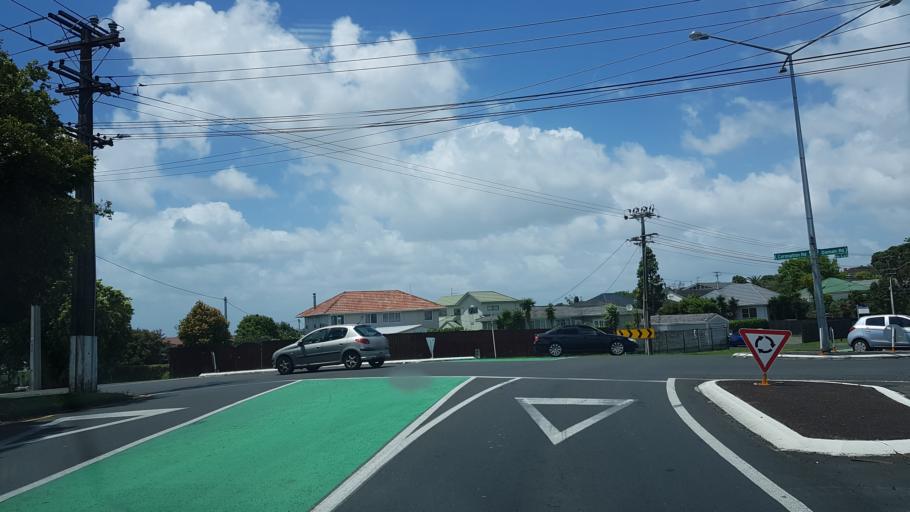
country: NZ
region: Auckland
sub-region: Auckland
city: North Shore
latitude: -36.7923
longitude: 174.7241
